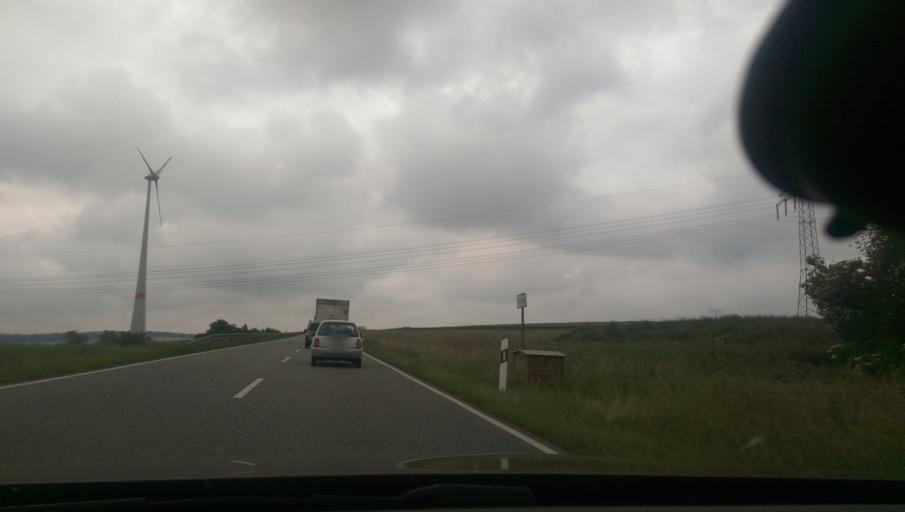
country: DE
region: Thuringia
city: Kleinfurra
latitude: 51.4328
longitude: 10.7957
